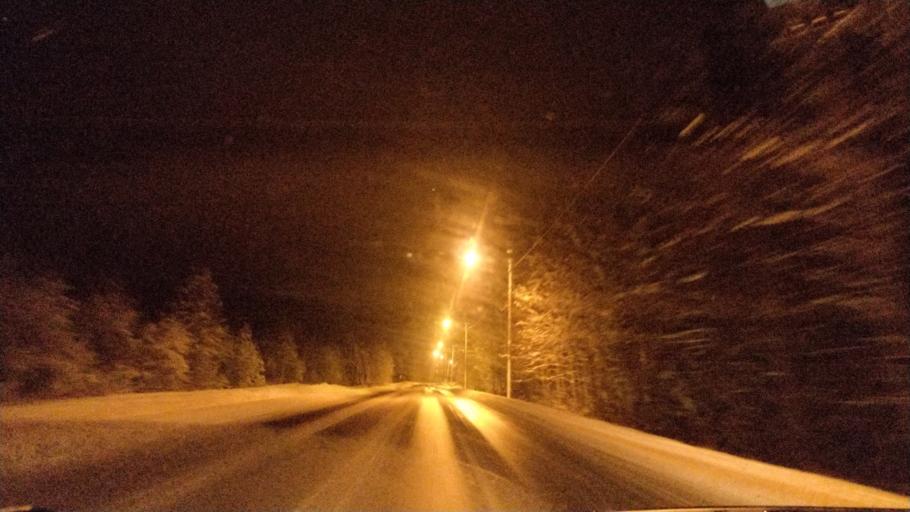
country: FI
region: Lapland
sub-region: Rovaniemi
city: Rovaniemi
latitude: 66.4012
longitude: 25.3888
